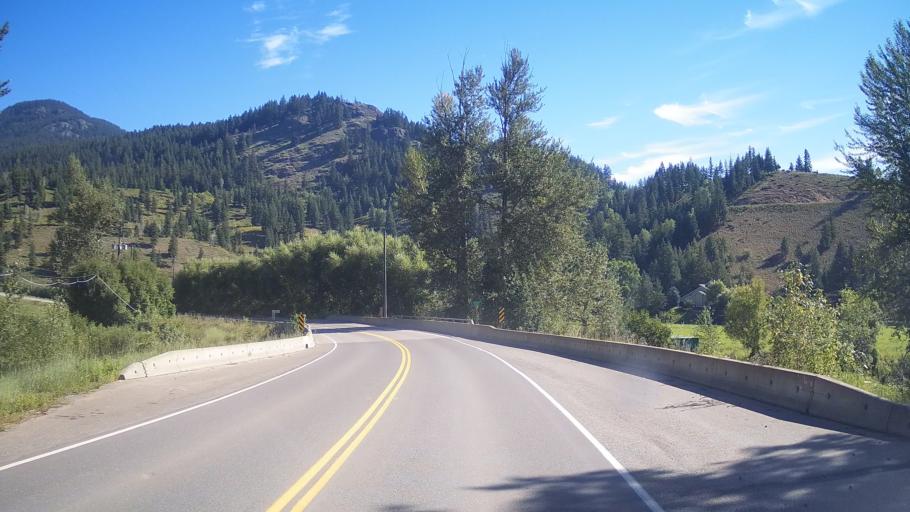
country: CA
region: British Columbia
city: Kamloops
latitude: 51.4318
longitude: -120.2086
